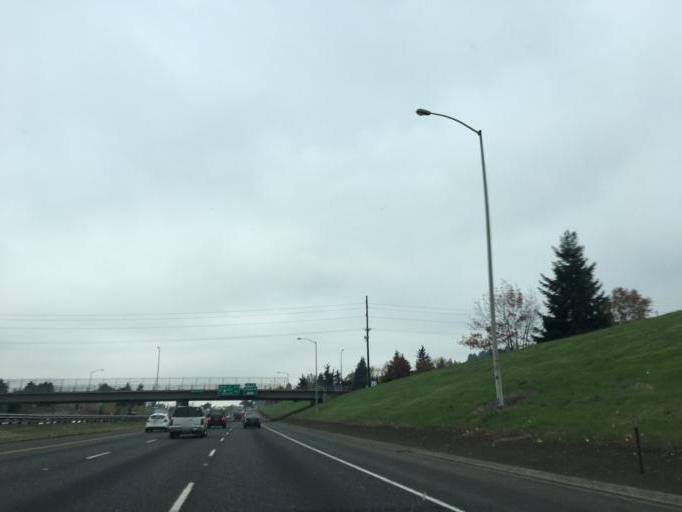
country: US
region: Oregon
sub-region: Multnomah County
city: Lents
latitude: 45.4884
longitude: -122.5660
